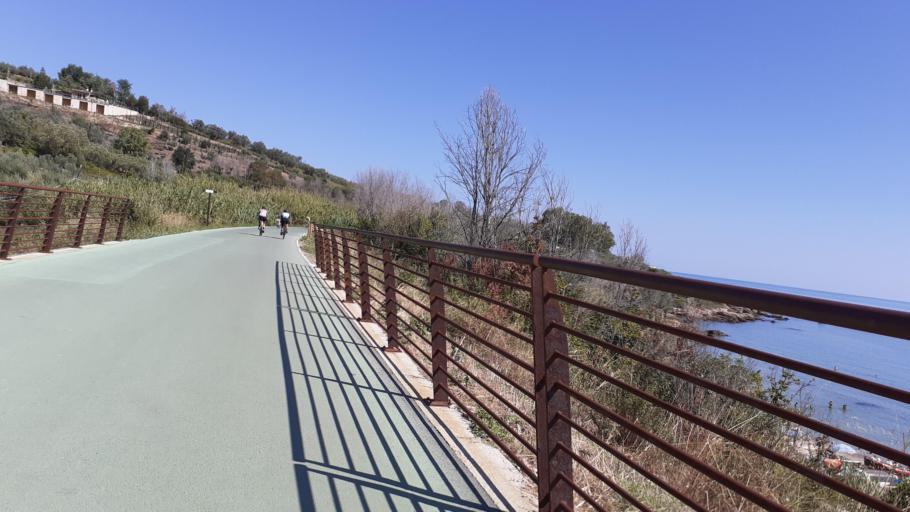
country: IT
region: Abruzzo
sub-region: Provincia di Chieti
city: Vasto
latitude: 42.1188
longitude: 14.7194
